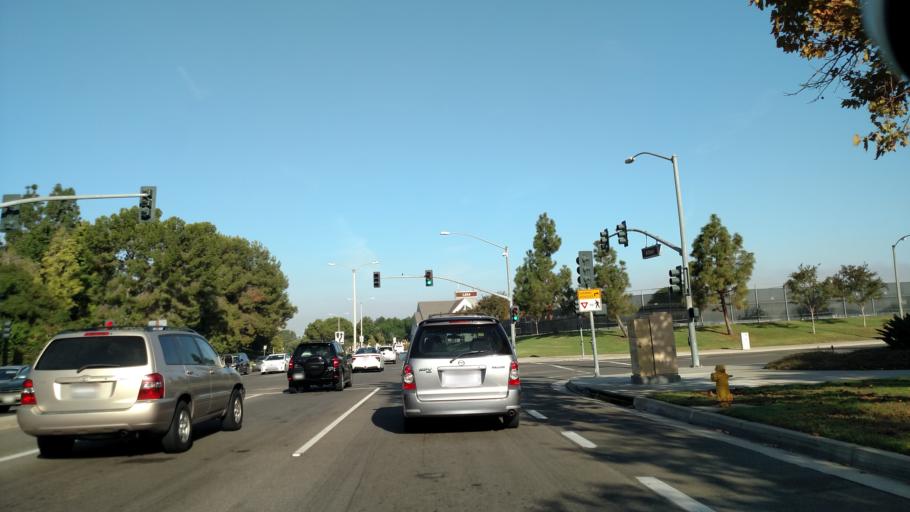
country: US
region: California
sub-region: Orange County
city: Irvine
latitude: 33.6758
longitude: -117.8043
